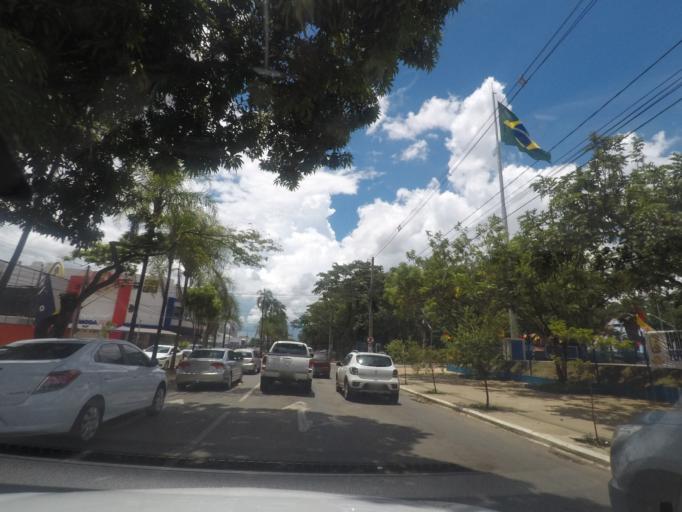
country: BR
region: Goias
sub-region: Goiania
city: Goiania
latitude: -16.6625
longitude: -49.2548
